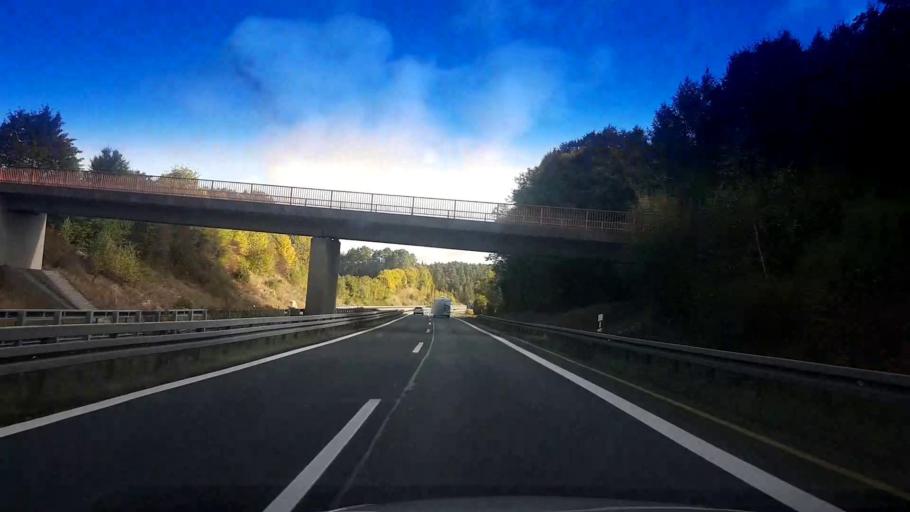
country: DE
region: Bavaria
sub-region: Upper Franconia
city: Wonsees
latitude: 50.0061
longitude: 11.2994
